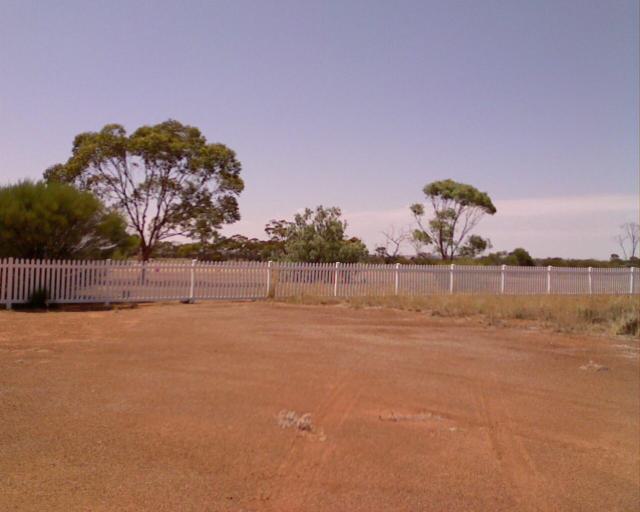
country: AU
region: Western Australia
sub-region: Merredin
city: Merredin
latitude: -30.9174
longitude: 118.2483
